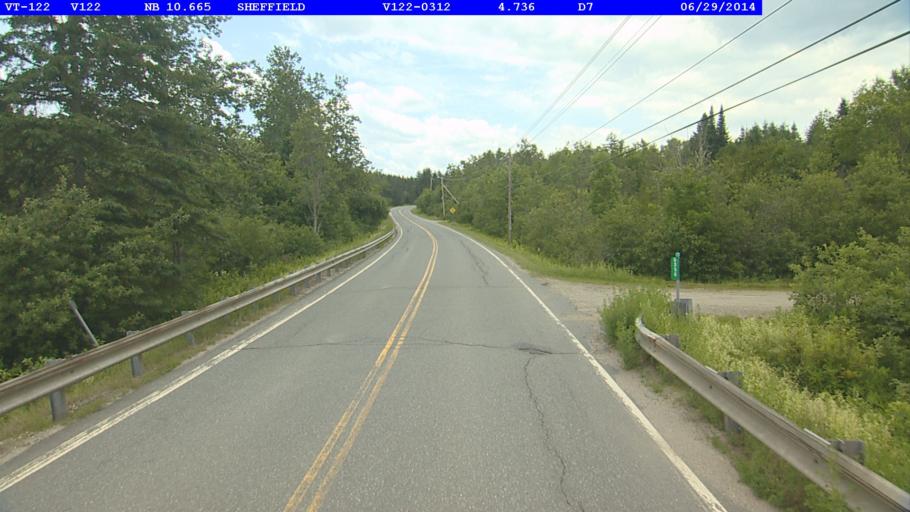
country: US
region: Vermont
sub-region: Caledonia County
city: Lyndonville
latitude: 44.6392
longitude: -72.1510
